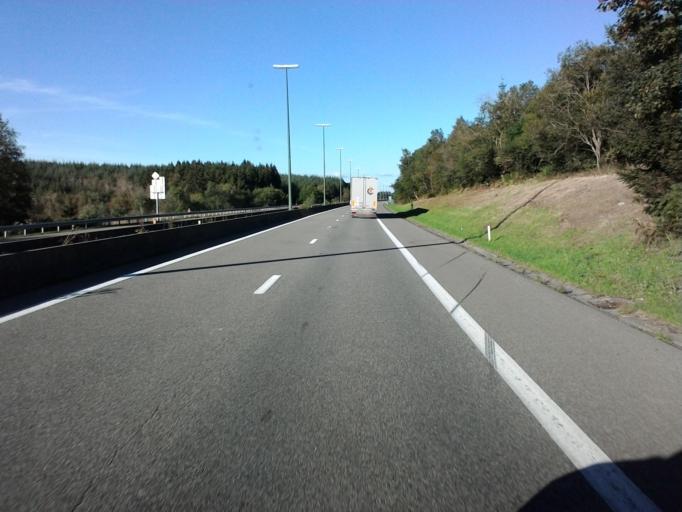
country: BE
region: Wallonia
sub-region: Province du Luxembourg
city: Bastogne
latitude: 50.0366
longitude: 5.7040
